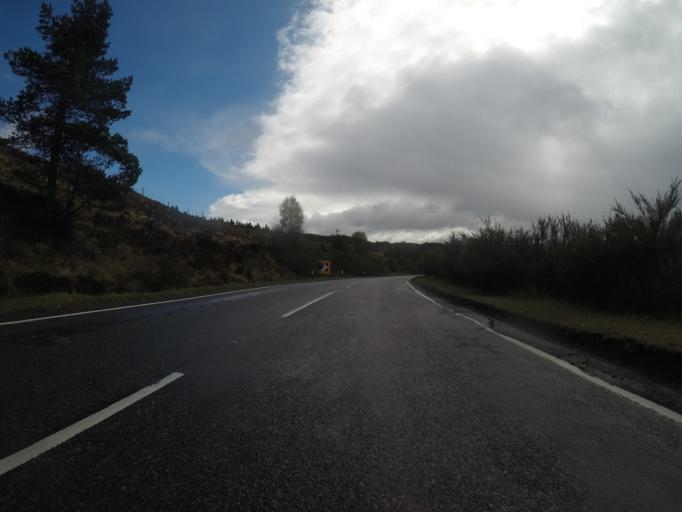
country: GB
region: Scotland
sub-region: Highland
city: Spean Bridge
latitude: 57.0876
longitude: -4.9674
